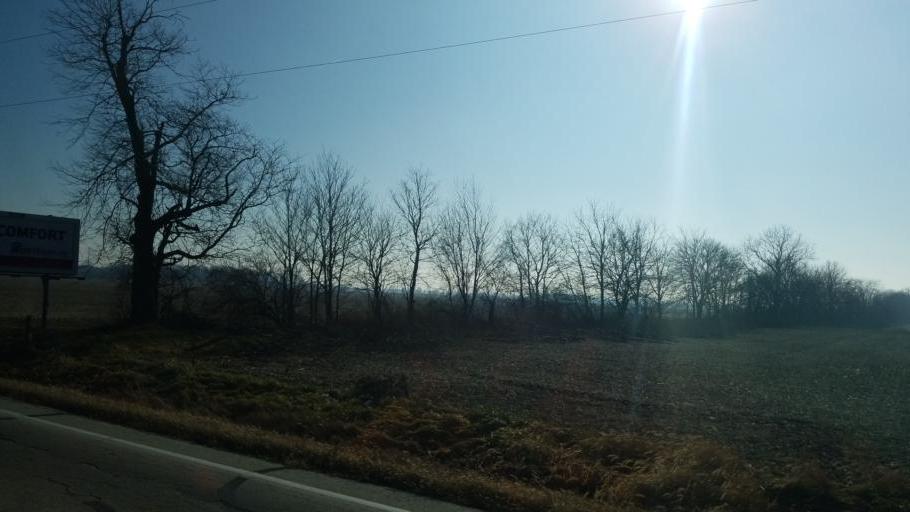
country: US
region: Ohio
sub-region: Seneca County
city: Tiffin
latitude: 41.1243
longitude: -83.1360
